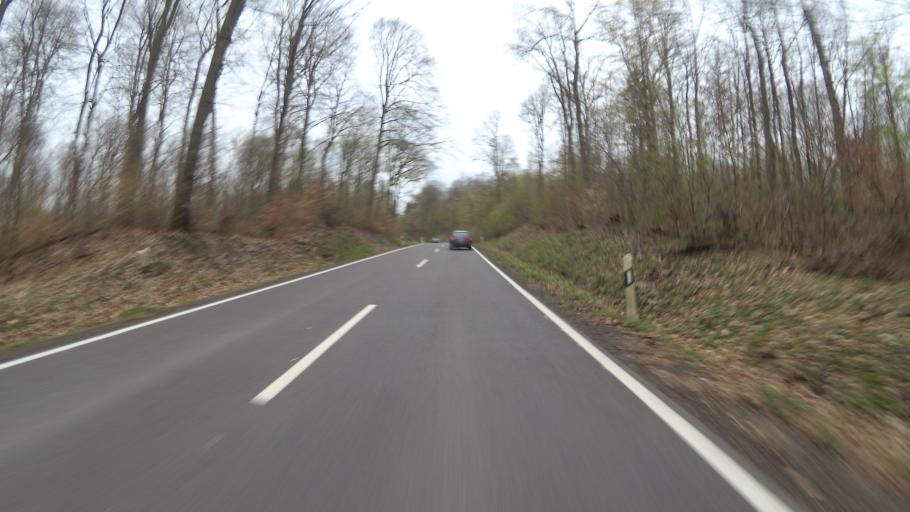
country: DE
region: Saarland
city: Friedrichsthal
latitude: 49.3019
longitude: 7.0879
